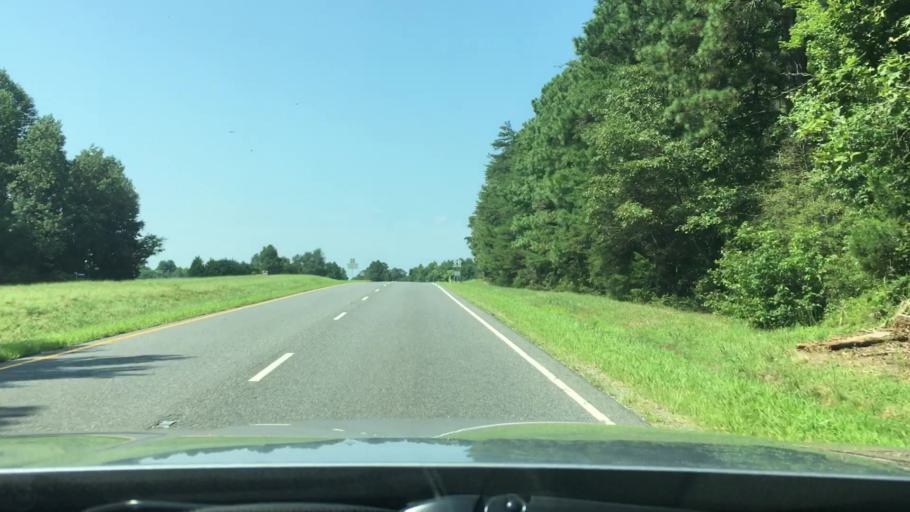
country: US
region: Virginia
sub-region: Caroline County
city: Bowling Green
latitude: 37.9639
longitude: -77.4324
